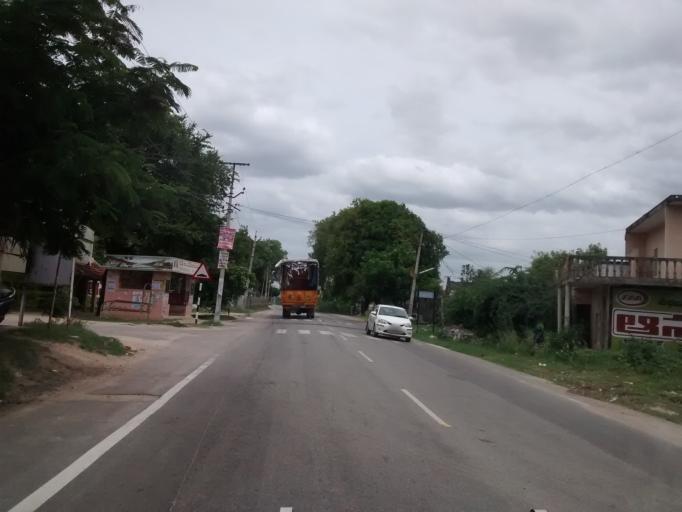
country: IN
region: Andhra Pradesh
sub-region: Chittoor
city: Chittoor
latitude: 13.2866
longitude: 79.0398
